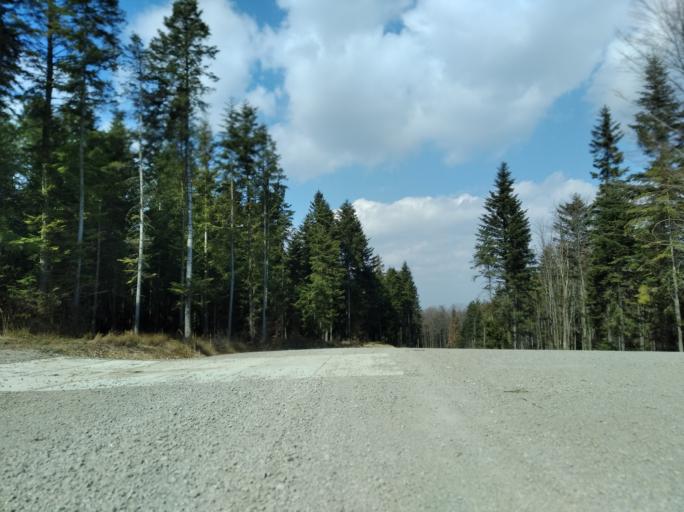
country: PL
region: Subcarpathian Voivodeship
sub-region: Powiat strzyzowski
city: Strzyzow
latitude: 49.8223
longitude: 21.8010
